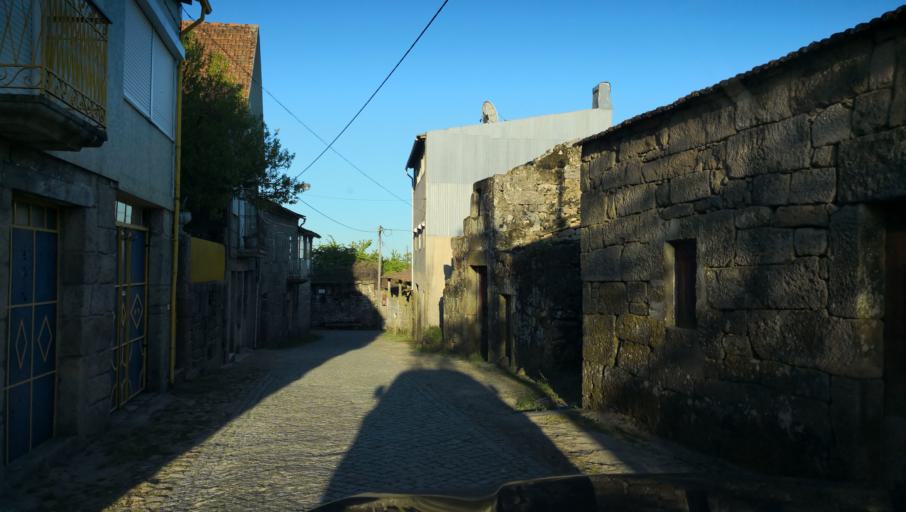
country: PT
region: Vila Real
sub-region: Sabrosa
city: Sabrosa
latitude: 41.3500
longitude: -7.6189
